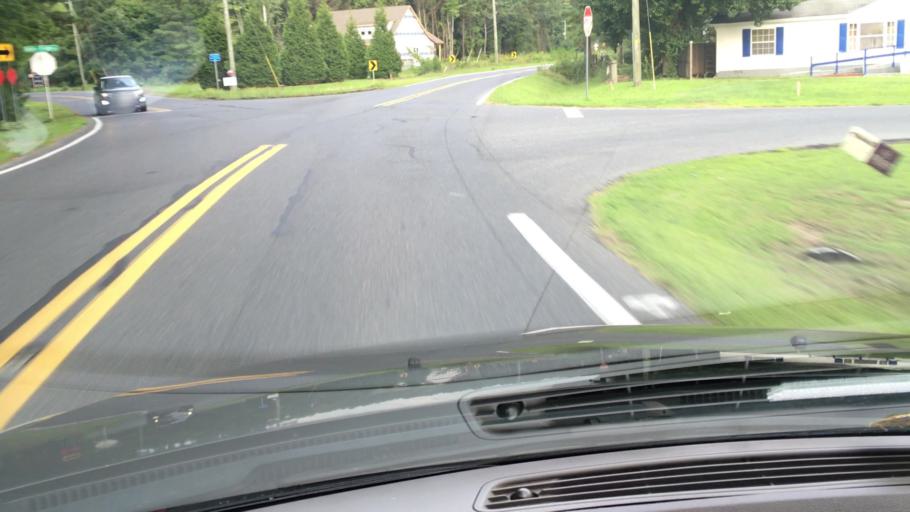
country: US
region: Delaware
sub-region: Sussex County
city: Ocean View
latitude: 38.5131
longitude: -75.1051
